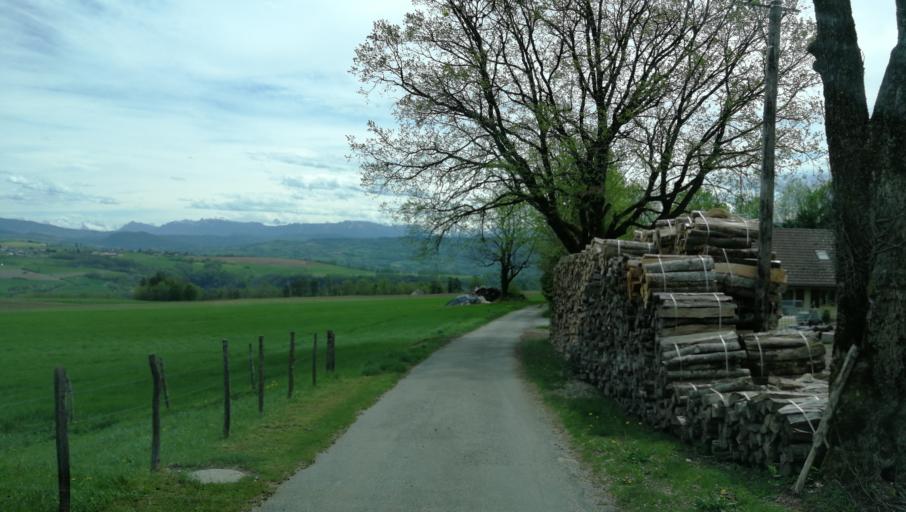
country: FR
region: Rhone-Alpes
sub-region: Departement de l'Ain
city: Bellegarde-sur-Valserine
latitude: 46.0110
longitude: 5.7783
